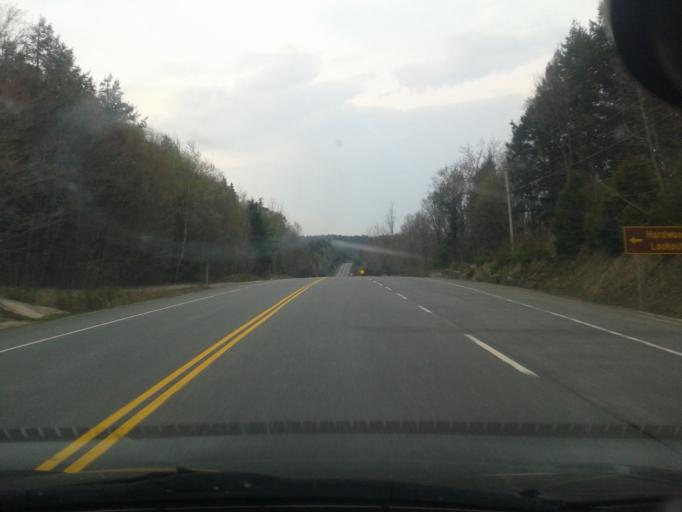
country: CA
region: Ontario
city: Huntsville
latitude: 45.5286
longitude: -78.7053
